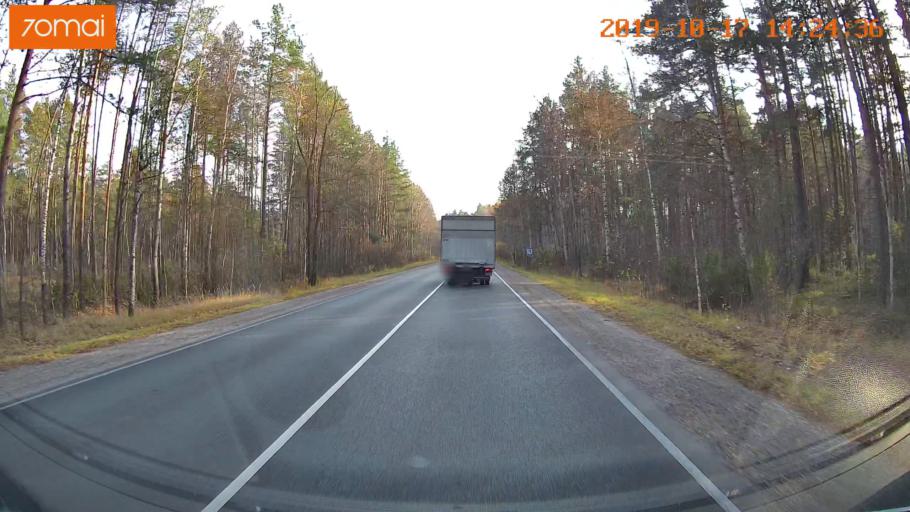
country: RU
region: Moskovskaya
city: Radovitskiy
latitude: 55.0079
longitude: 39.9698
